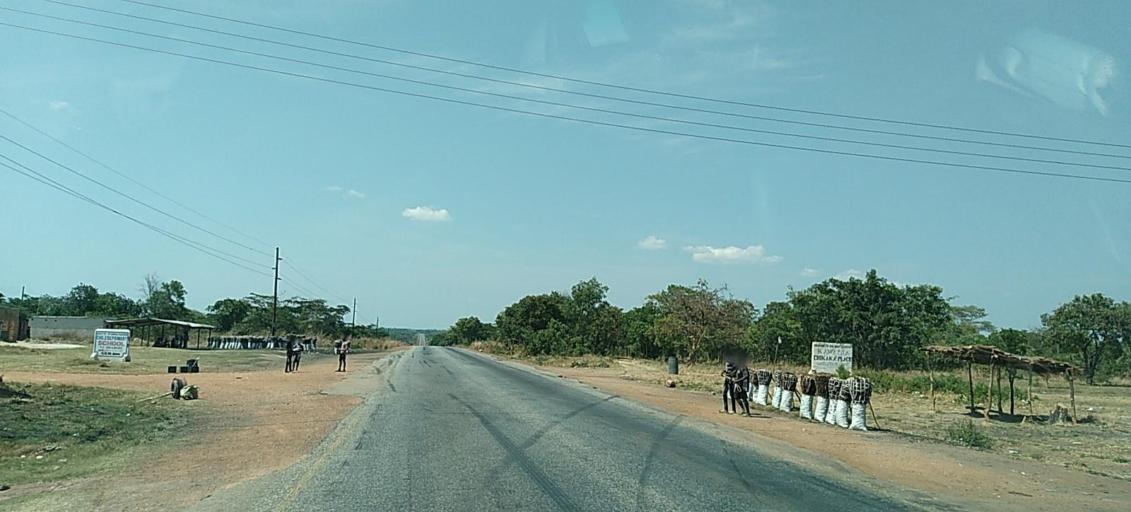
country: ZM
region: Central
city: Kapiri Mposhi
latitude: -13.5395
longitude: 28.6452
